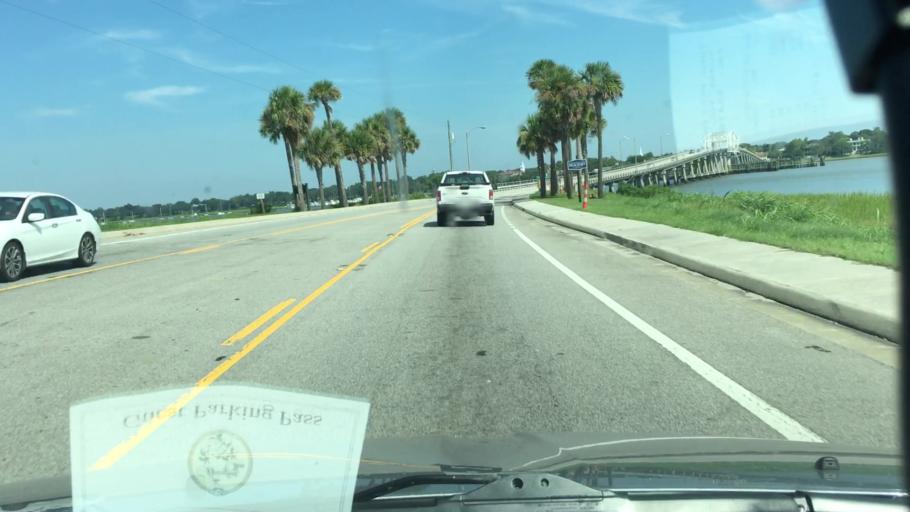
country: US
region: South Carolina
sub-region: Beaufort County
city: Beaufort
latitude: 32.4232
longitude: -80.6676
